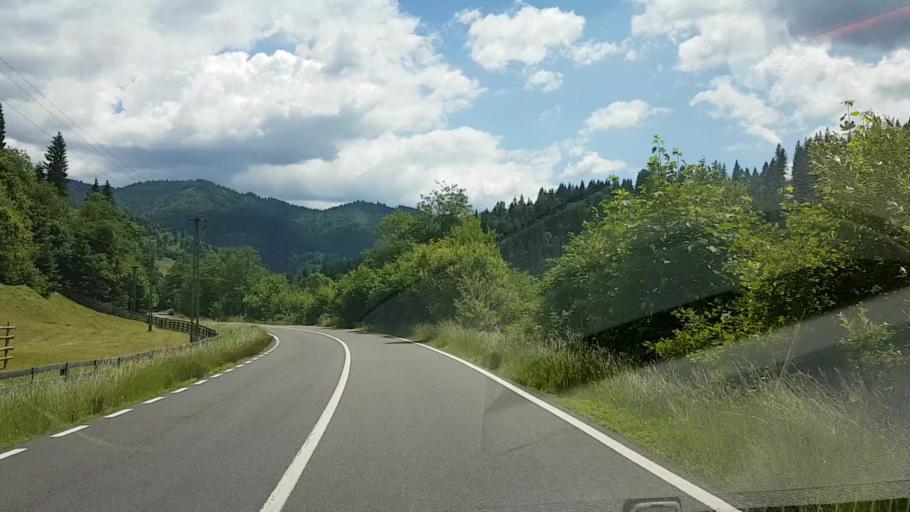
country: RO
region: Suceava
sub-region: Comuna Crucea
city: Crucea
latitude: 47.3945
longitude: 25.5652
